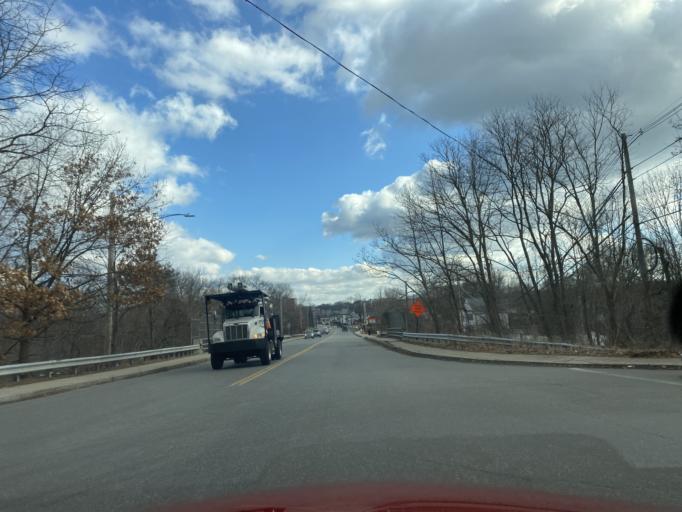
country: US
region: Massachusetts
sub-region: Middlesex County
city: Woburn
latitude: 42.4804
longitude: -71.1274
